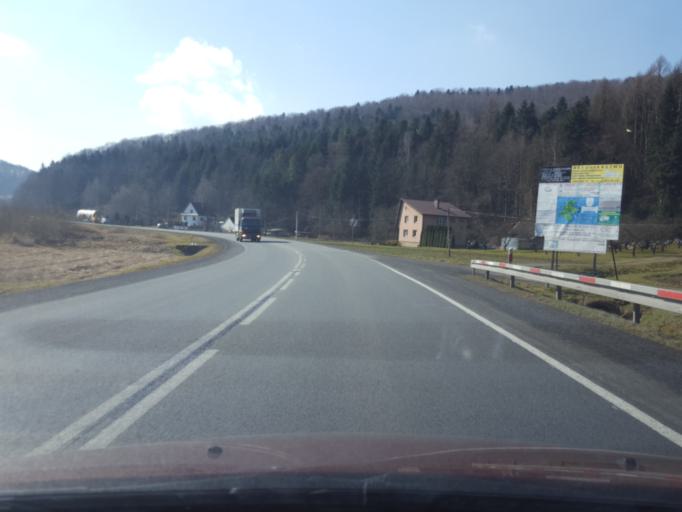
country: PL
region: Lesser Poland Voivodeship
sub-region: Powiat nowosadecki
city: Lososina Dolna
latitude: 49.7793
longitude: 20.6417
